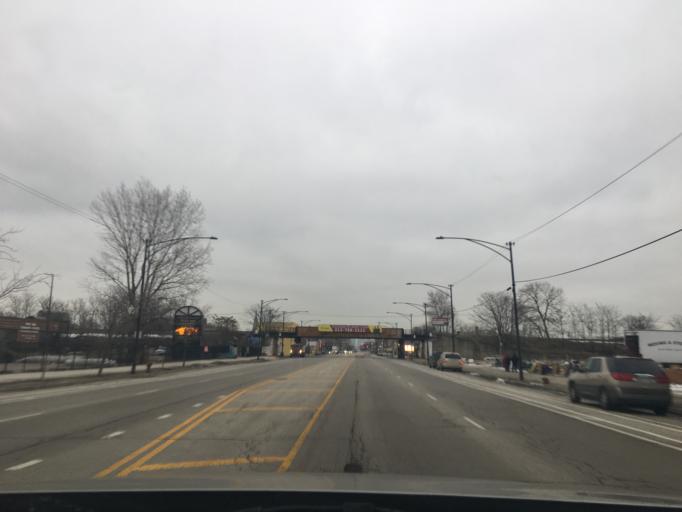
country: US
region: Illinois
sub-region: Cook County
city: Cicero
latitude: 41.8806
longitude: -87.7416
